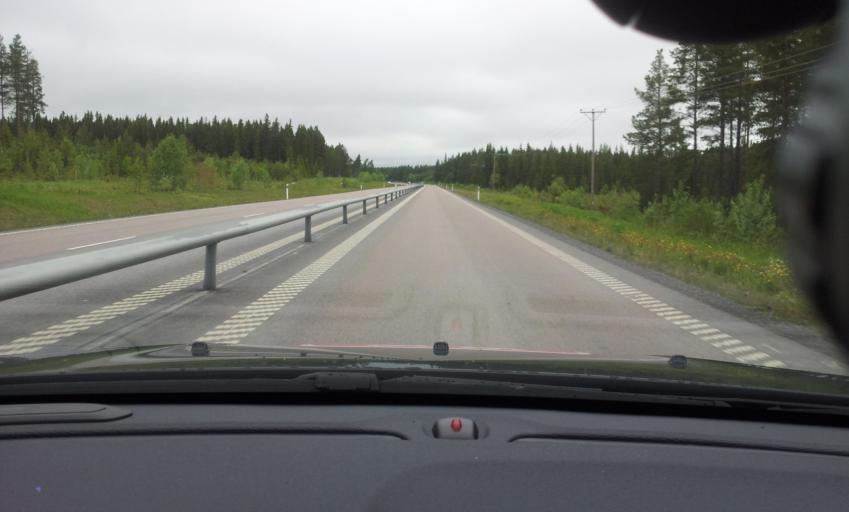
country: SE
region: Jaemtland
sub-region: OEstersunds Kommun
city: Ostersund
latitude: 63.2392
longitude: 14.6029
